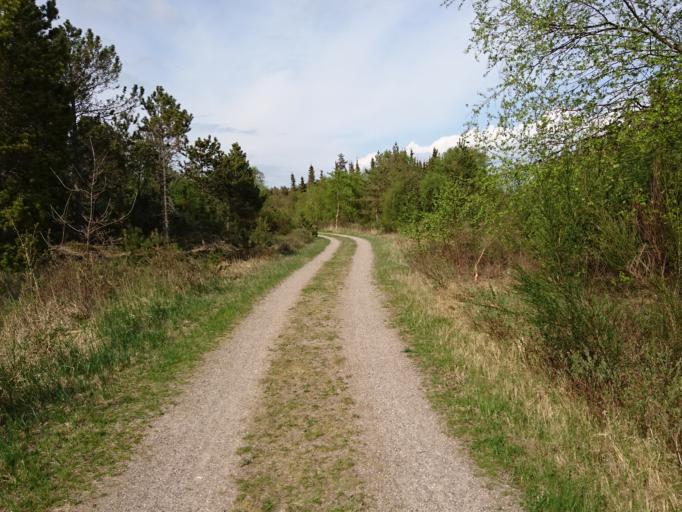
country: DK
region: North Denmark
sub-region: Frederikshavn Kommune
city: Skagen
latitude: 57.7116
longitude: 10.5131
